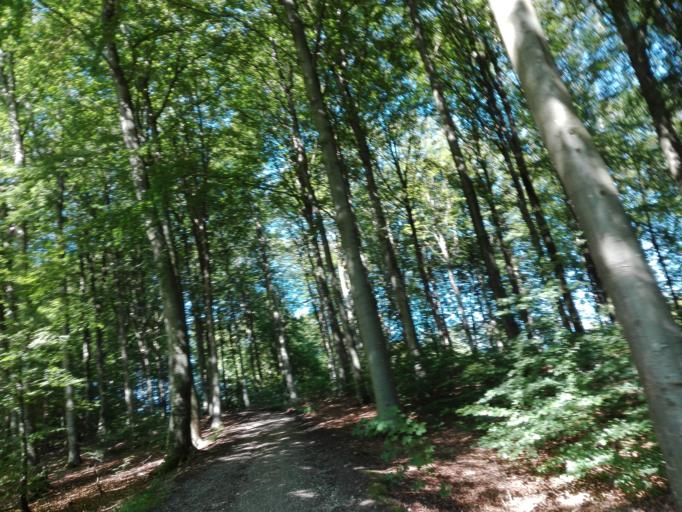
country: DK
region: Central Jutland
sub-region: Odder Kommune
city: Odder
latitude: 55.9507
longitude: 10.1502
